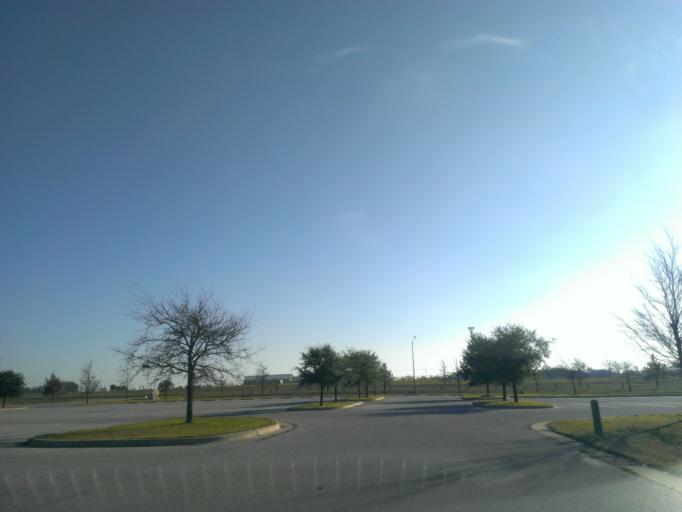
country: US
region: Texas
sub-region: Williamson County
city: Round Rock
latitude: 30.5414
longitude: -97.6194
